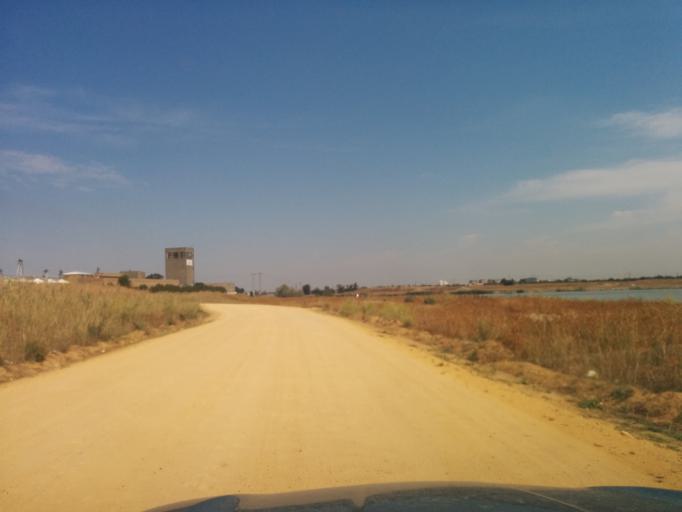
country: ES
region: Andalusia
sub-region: Provincia de Sevilla
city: Gelves
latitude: 37.3210
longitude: -5.9934
